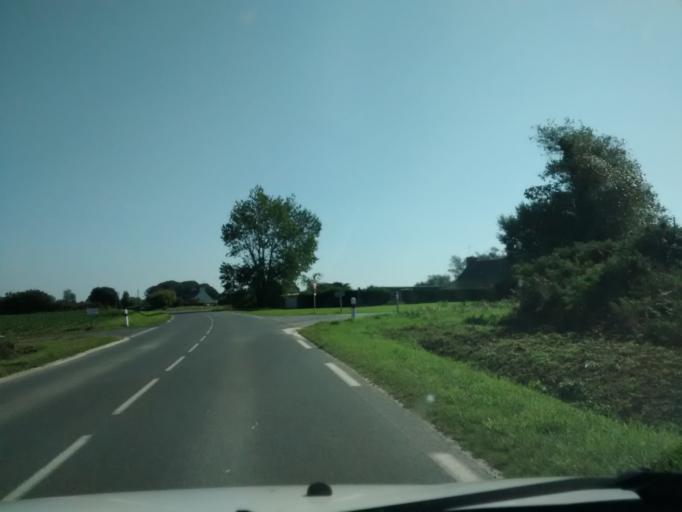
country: FR
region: Brittany
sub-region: Departement des Cotes-d'Armor
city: Pleubian
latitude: 48.8303
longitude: -3.1616
